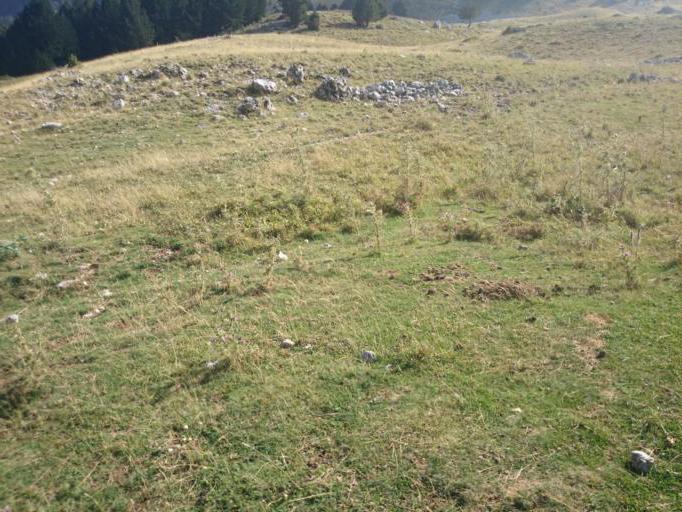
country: AL
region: Elbasan
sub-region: Rrethi i Gramshit
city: Kushove
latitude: 40.7329
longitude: 20.1497
